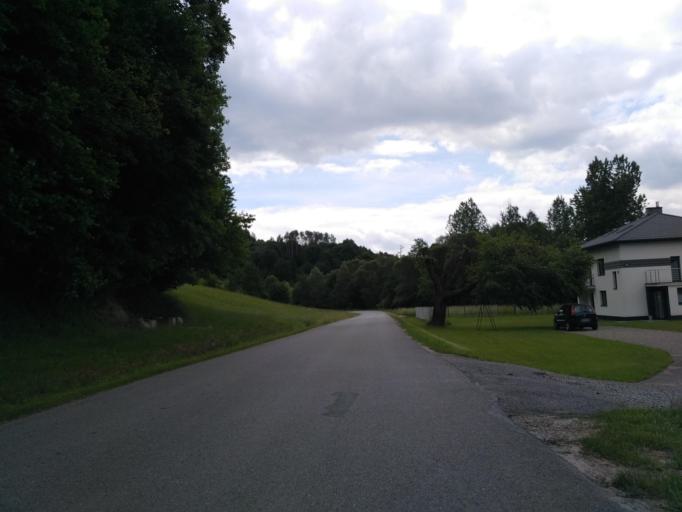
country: PL
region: Subcarpathian Voivodeship
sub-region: Powiat przeworski
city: Jawornik Polski
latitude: 49.8502
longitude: 22.3036
